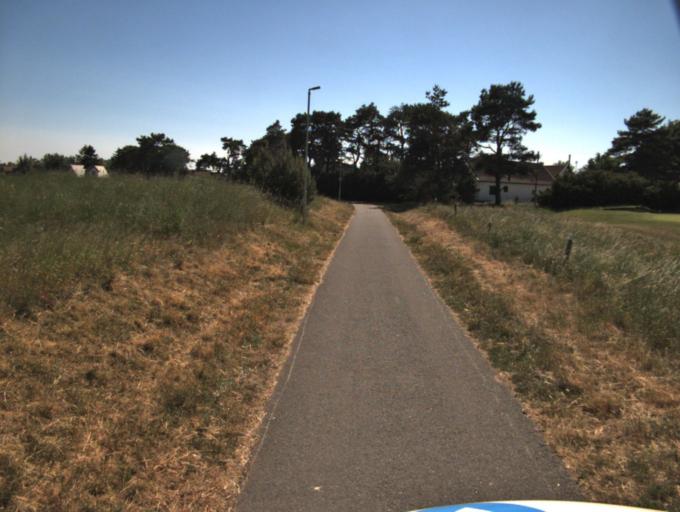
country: SE
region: Skane
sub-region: Kristianstads Kommun
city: Ahus
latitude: 55.9214
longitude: 14.2820
